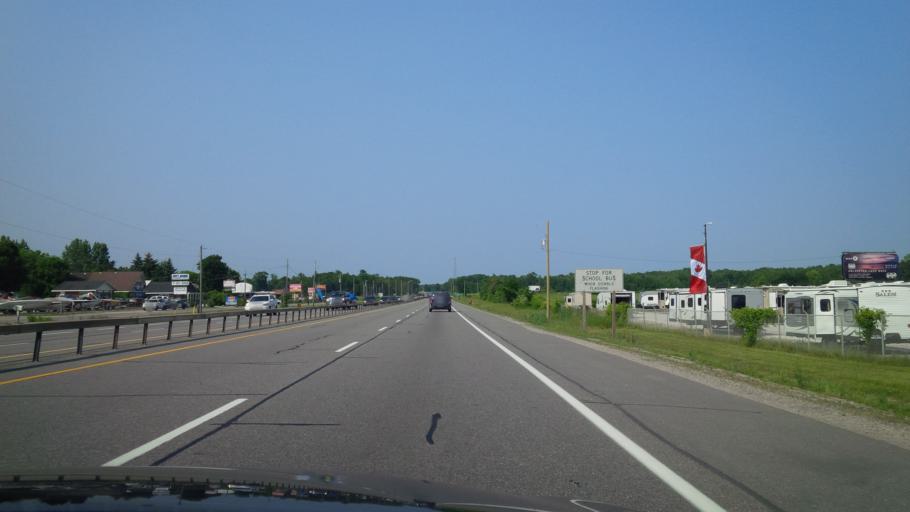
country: CA
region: Ontario
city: Orillia
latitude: 44.5030
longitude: -79.4853
